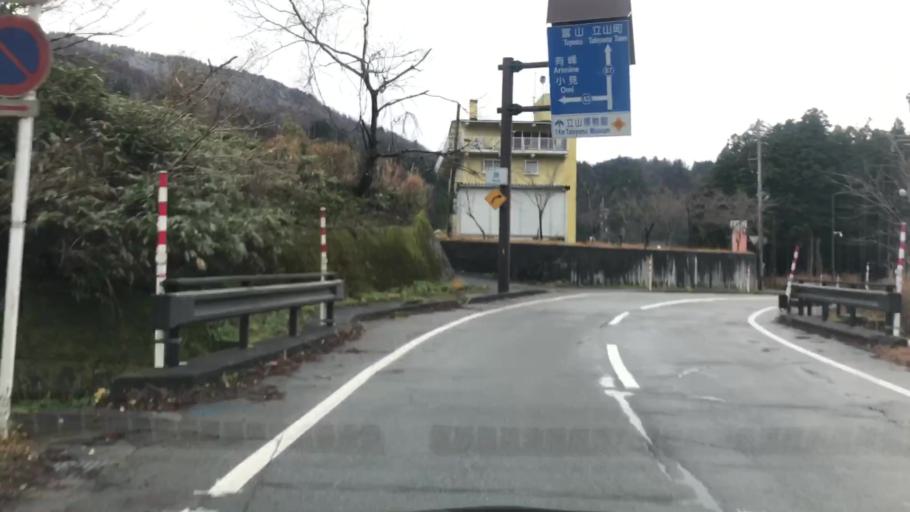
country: JP
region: Toyama
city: Kamiichi
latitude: 36.5769
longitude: 137.4195
